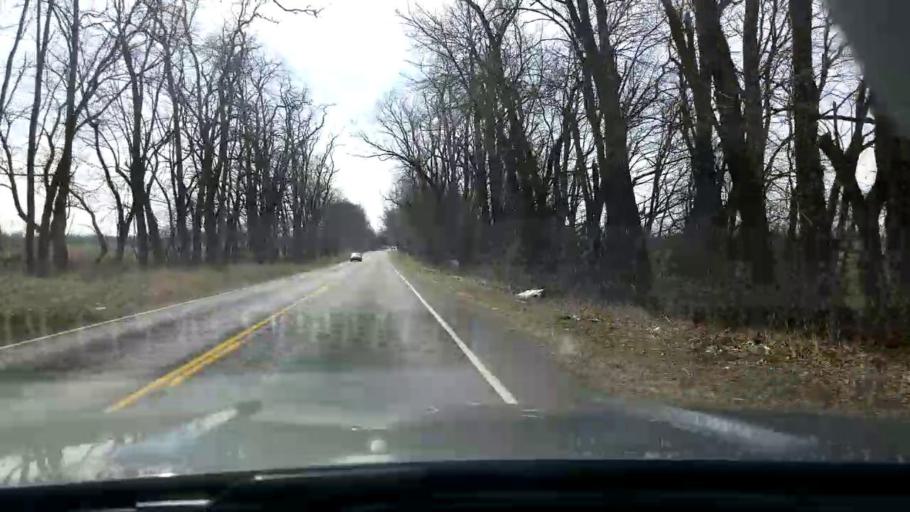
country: US
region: Michigan
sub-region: Jackson County
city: Spring Arbor
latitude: 42.1730
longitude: -84.5201
